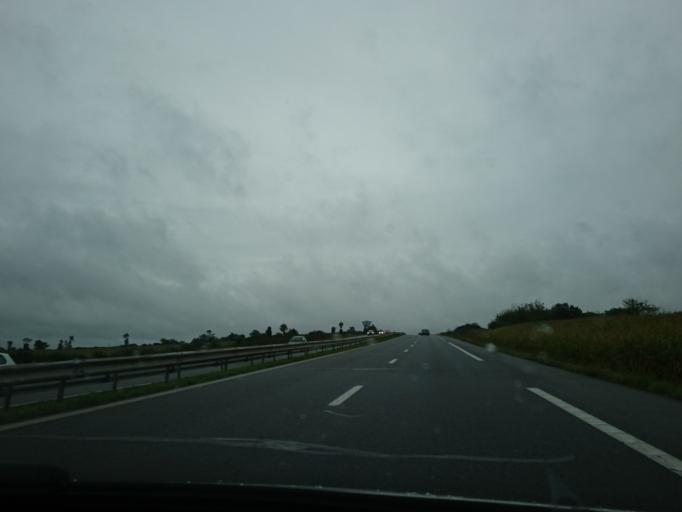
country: FR
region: Brittany
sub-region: Departement du Morbihan
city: Muzillac
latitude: 47.5428
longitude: -2.4306
